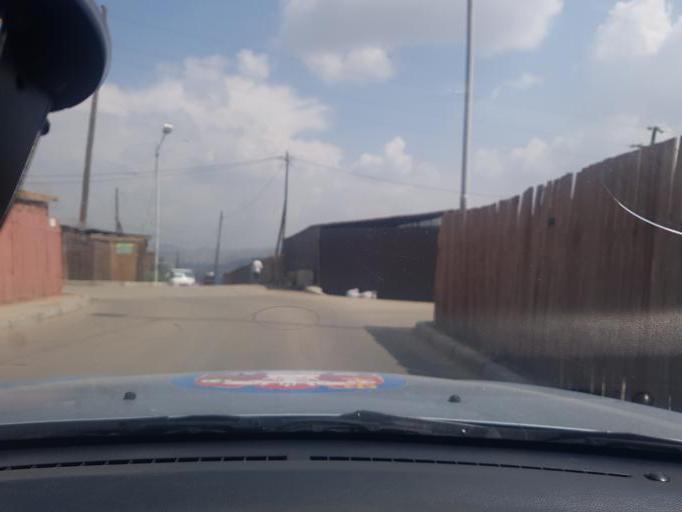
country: MN
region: Ulaanbaatar
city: Ulaanbaatar
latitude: 47.9347
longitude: 106.8952
